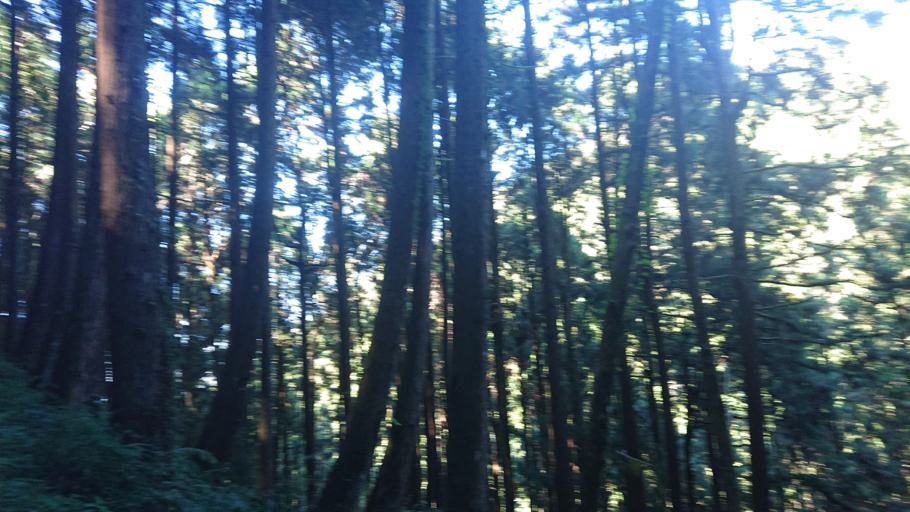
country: TW
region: Taiwan
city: Lugu
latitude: 23.4838
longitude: 120.8286
